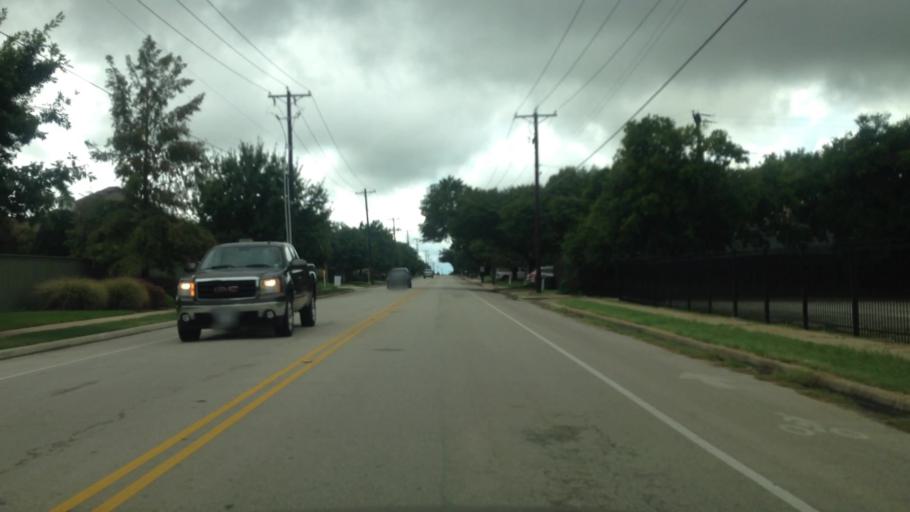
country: US
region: Texas
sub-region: Tarrant County
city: Crowley
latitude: 32.6281
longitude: -97.3918
